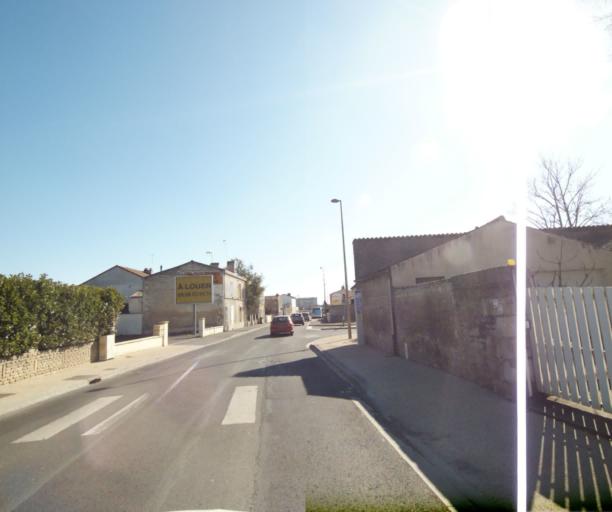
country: FR
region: Poitou-Charentes
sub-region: Departement des Deux-Sevres
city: Niort
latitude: 46.3367
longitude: -0.4731
